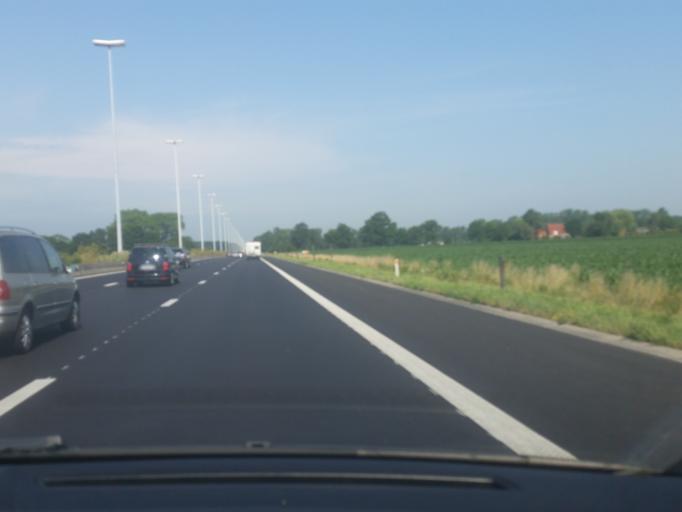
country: BE
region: Flanders
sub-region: Provincie Oost-Vlaanderen
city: Aalter
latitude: 51.0893
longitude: 3.4143
